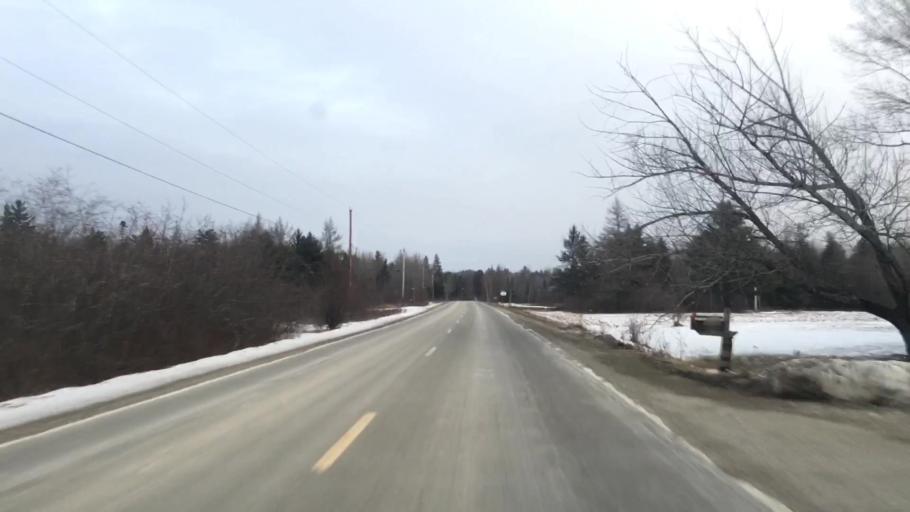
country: US
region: Maine
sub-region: Hancock County
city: Franklin
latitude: 44.6925
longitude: -68.3472
